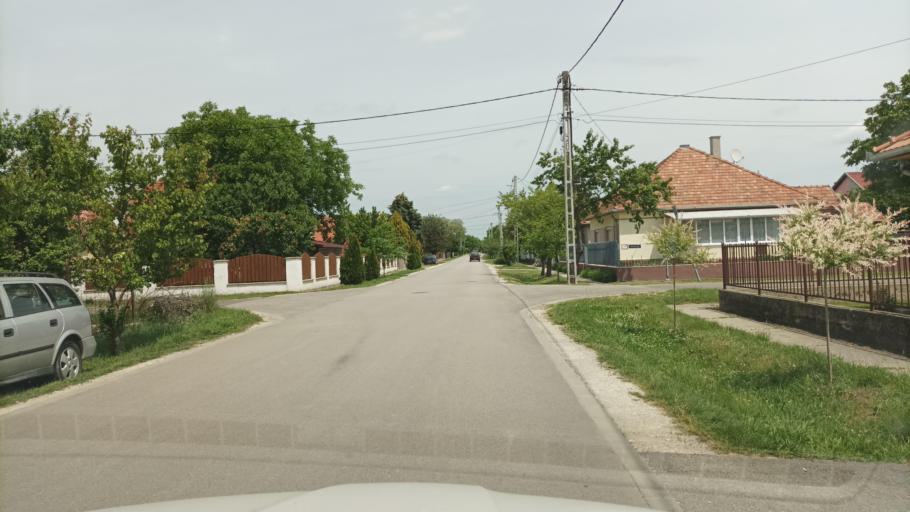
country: HU
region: Pest
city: Szigethalom
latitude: 47.3176
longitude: 18.9902
